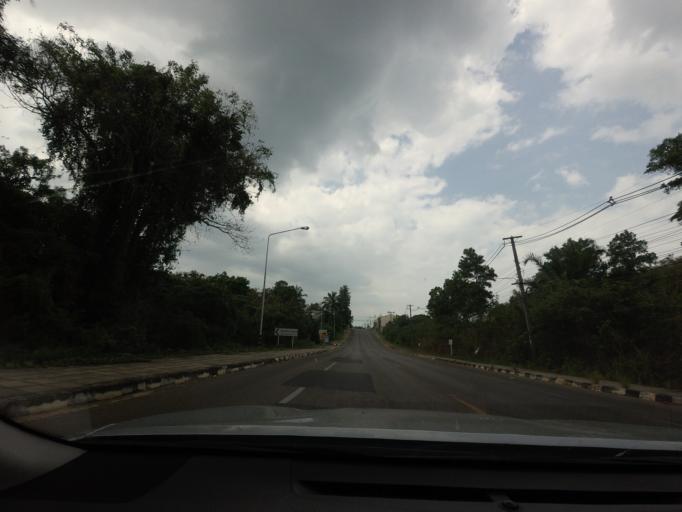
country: TH
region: Phangnga
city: Ban Ao Nang
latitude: 8.0550
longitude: 98.7545
